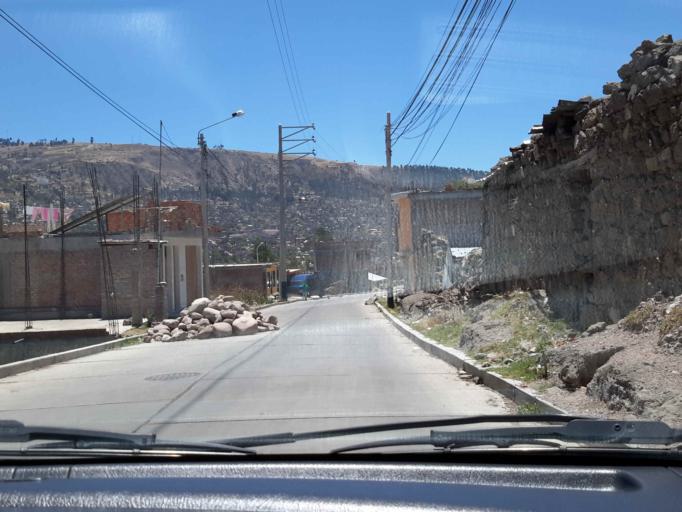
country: PE
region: Ayacucho
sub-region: Provincia de Huamanga
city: Carmen Alto
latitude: -13.1739
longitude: -74.2231
